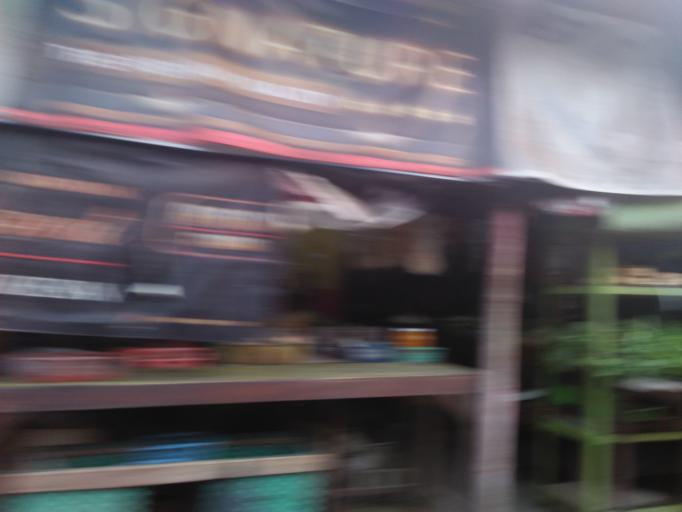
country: ID
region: Daerah Istimewa Yogyakarta
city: Sewon
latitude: -7.8563
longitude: 110.4098
